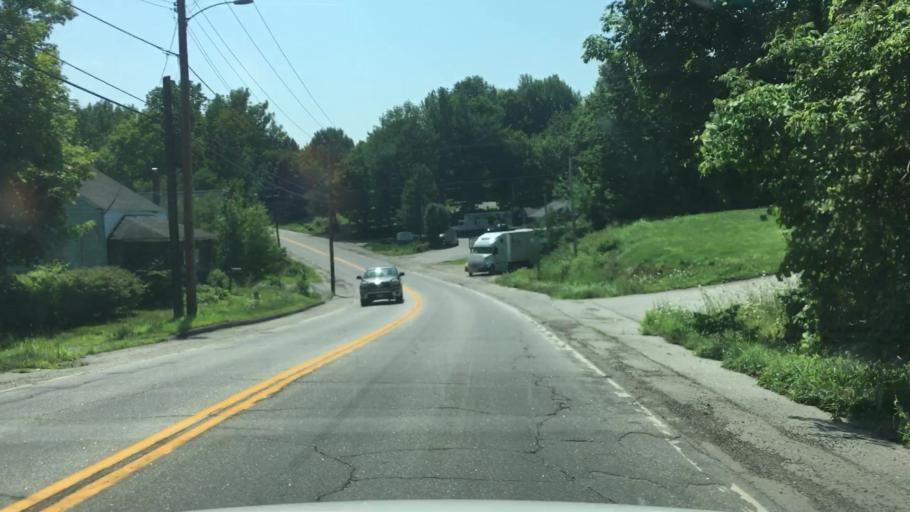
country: US
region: Maine
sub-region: Kennebec County
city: Hallowell
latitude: 44.2702
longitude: -69.7899
